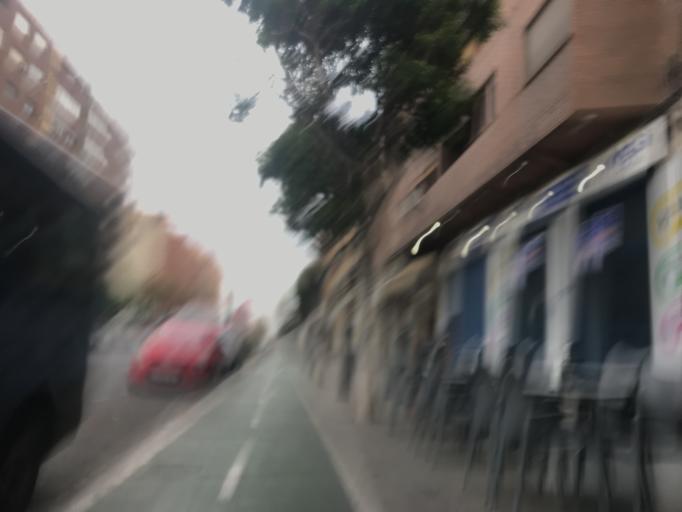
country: ES
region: Valencia
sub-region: Provincia de Valencia
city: Valencia
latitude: 39.4646
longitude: -0.3480
